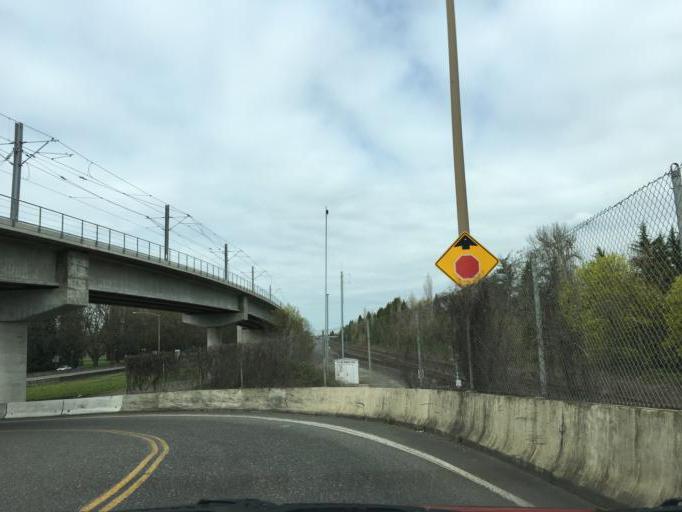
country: US
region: Oregon
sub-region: Clackamas County
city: Milwaukie
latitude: 45.4653
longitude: -122.6376
